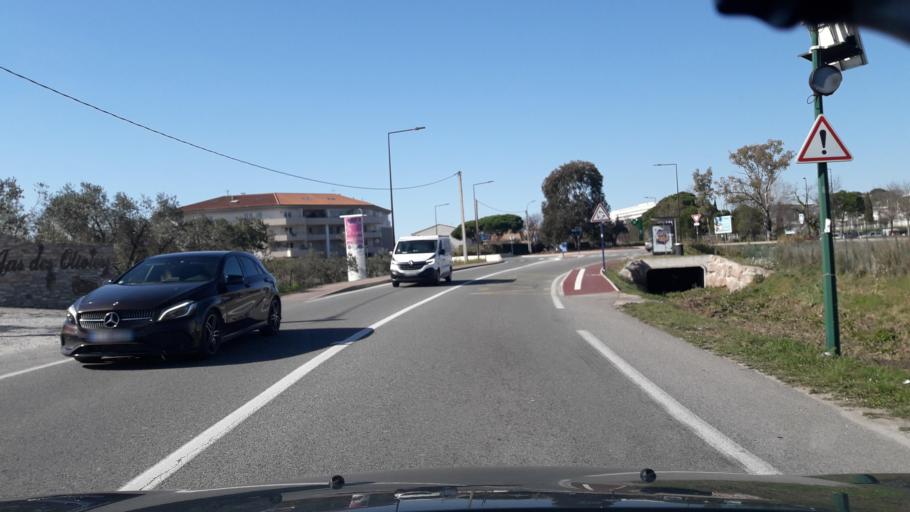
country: FR
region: Provence-Alpes-Cote d'Azur
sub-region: Departement du Var
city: Saint-Raphael
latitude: 43.4361
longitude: 6.7601
